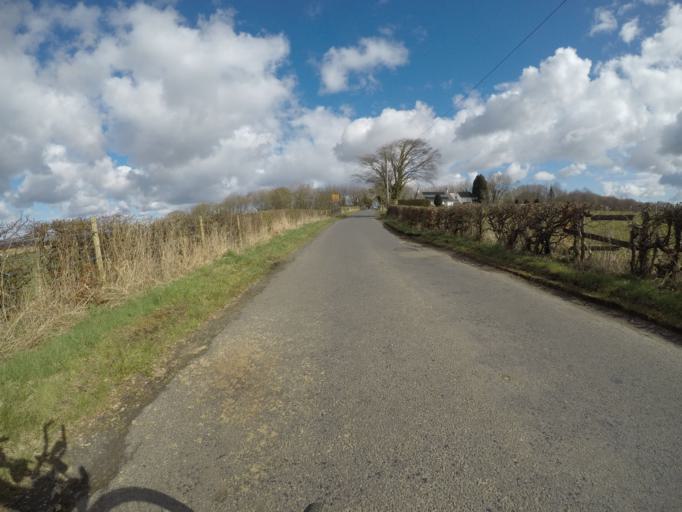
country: GB
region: Scotland
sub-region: North Ayrshire
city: Beith
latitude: 55.7181
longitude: -4.6198
